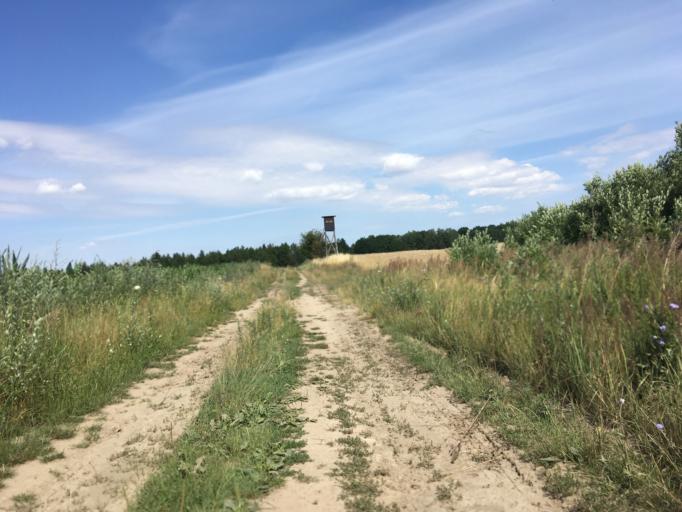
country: DE
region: Brandenburg
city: Casekow
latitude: 53.2254
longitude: 14.1371
